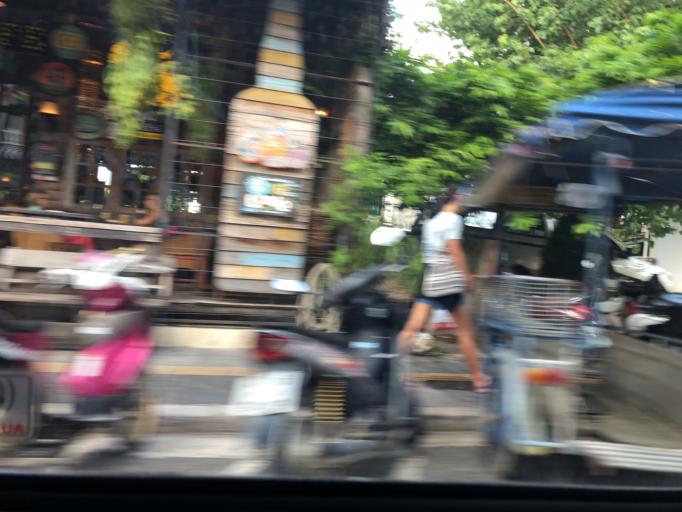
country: TH
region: Phuket
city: Ban Talat Nua
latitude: 7.8841
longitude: 98.3908
